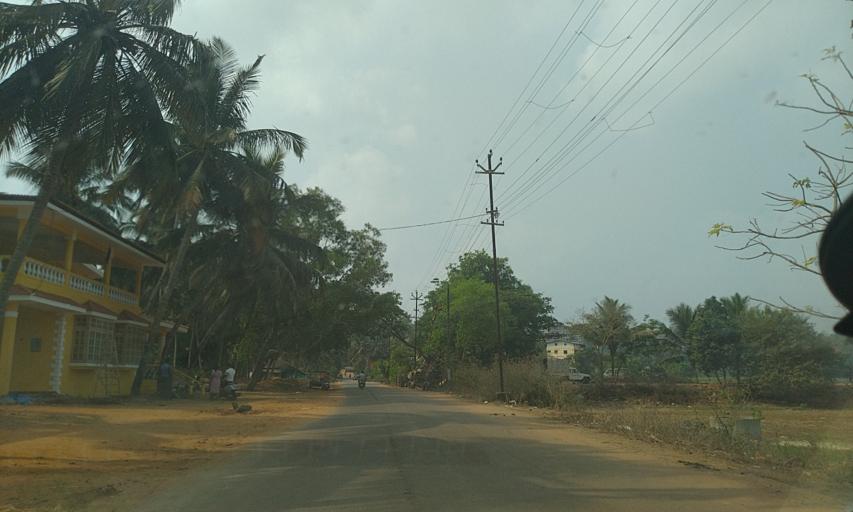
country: IN
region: Goa
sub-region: North Goa
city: Taleigao
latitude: 15.4680
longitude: 73.8278
